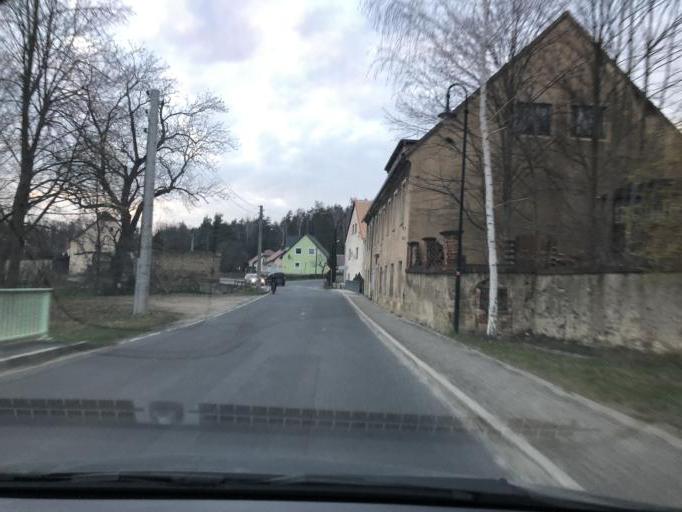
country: DE
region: Saxony
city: Neukirch
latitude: 51.2516
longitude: 13.9730
